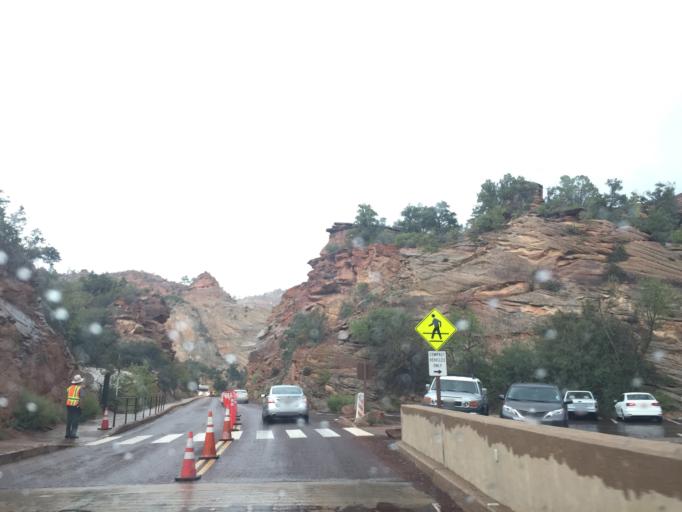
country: US
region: Utah
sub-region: Washington County
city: Hildale
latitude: 37.2132
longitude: -112.9408
